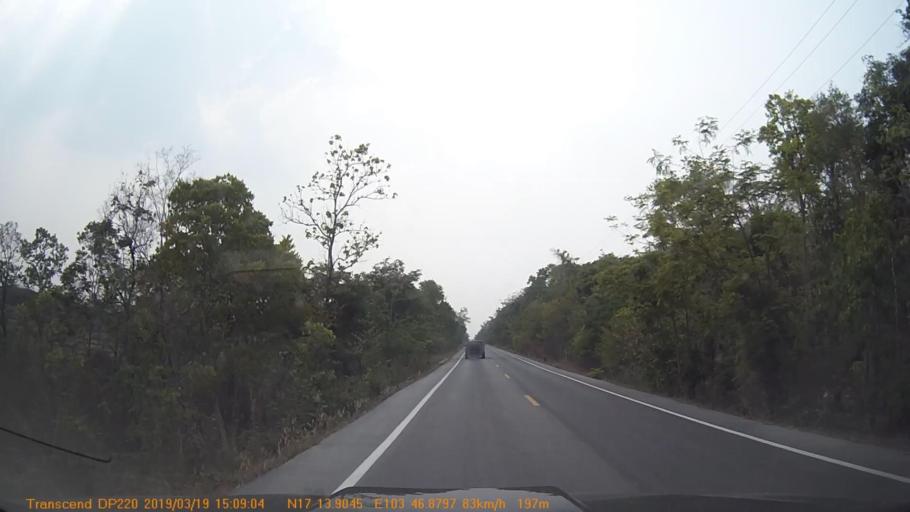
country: TH
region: Sakon Nakhon
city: Nikhom Nam Un
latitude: 17.2318
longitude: 103.7811
